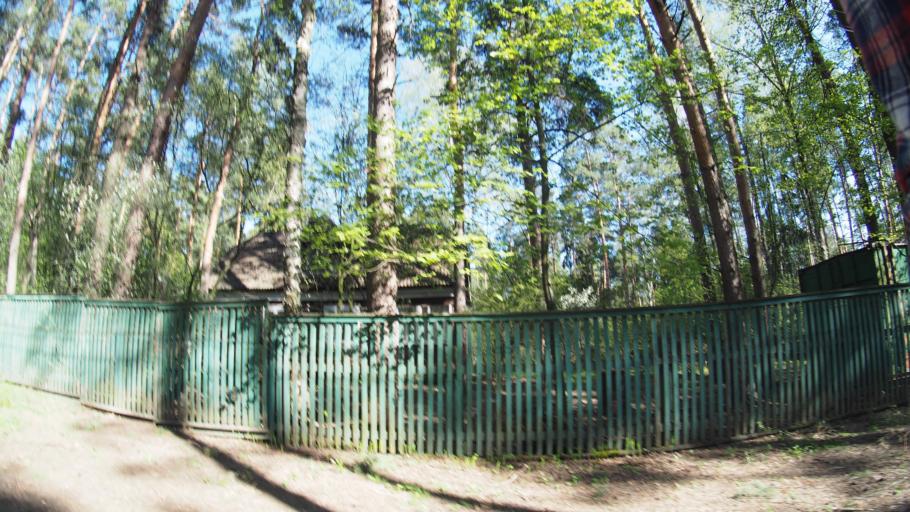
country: RU
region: Moskovskaya
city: Kratovo
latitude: 55.5876
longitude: 38.1831
